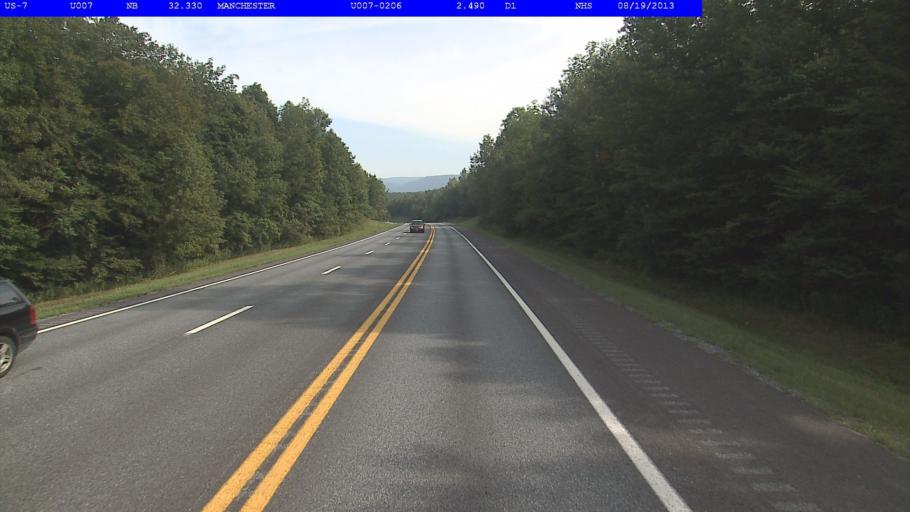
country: US
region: Vermont
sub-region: Bennington County
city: Manchester Center
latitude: 43.1461
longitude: -73.0503
